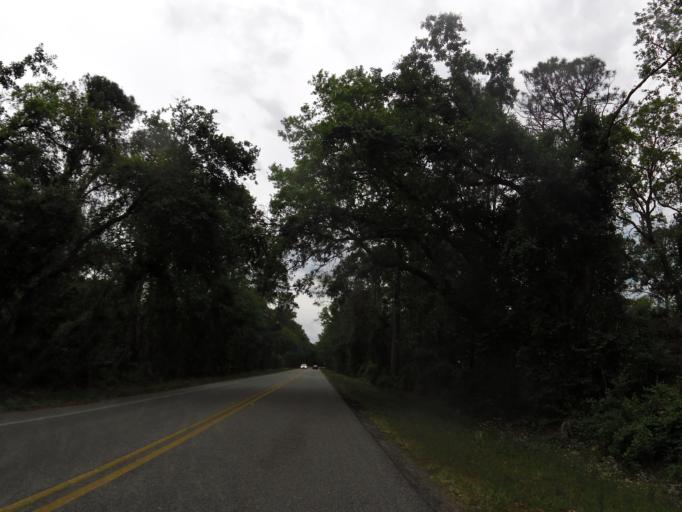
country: US
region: Florida
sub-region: Saint Johns County
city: Ponte Vedra Beach
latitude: 30.2249
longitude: -81.3974
